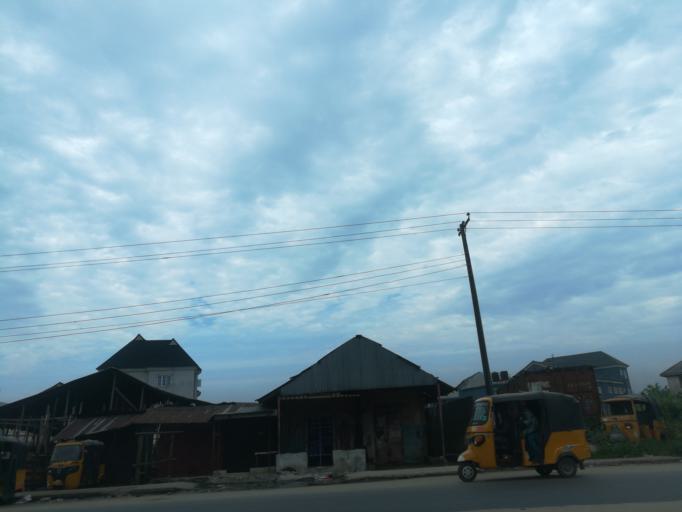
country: NG
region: Rivers
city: Port Harcourt
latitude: 4.8141
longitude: 6.9497
